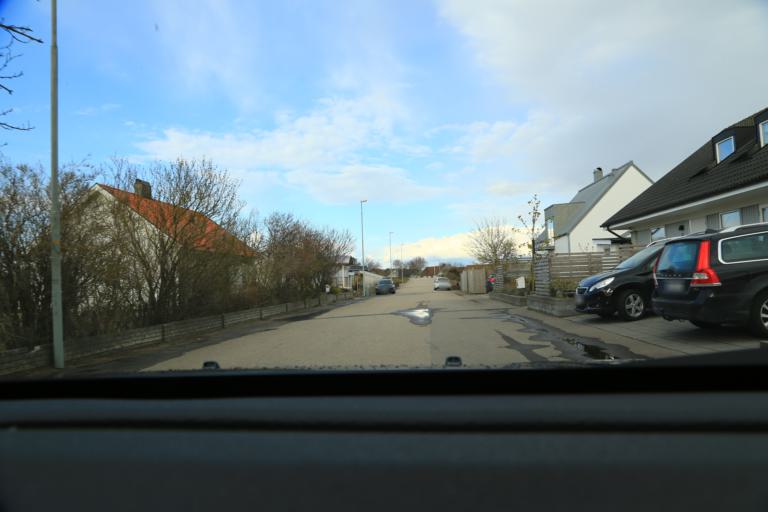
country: SE
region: Halland
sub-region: Varbergs Kommun
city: Traslovslage
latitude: 57.0502
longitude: 12.2787
